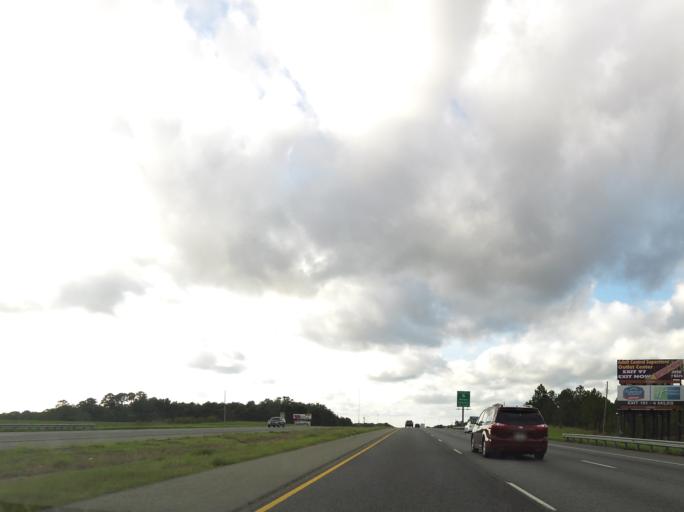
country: US
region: Georgia
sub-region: Crisp County
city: Cordele
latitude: 31.8971
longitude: -83.7336
